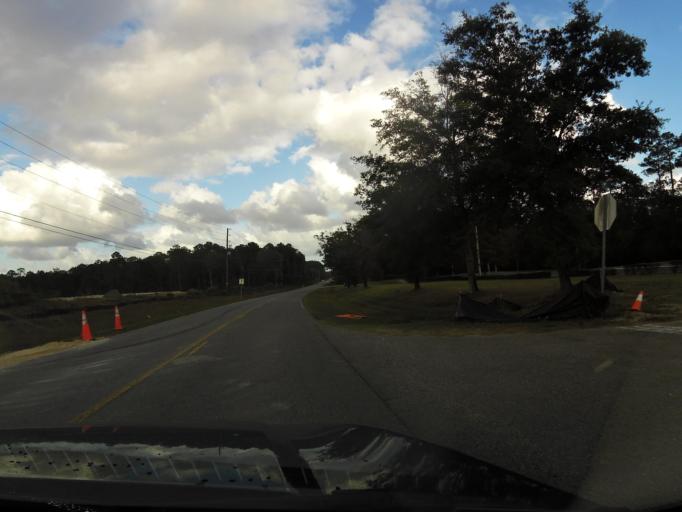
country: US
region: Florida
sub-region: Clay County
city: Asbury Lake
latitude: 30.0505
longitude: -81.7648
